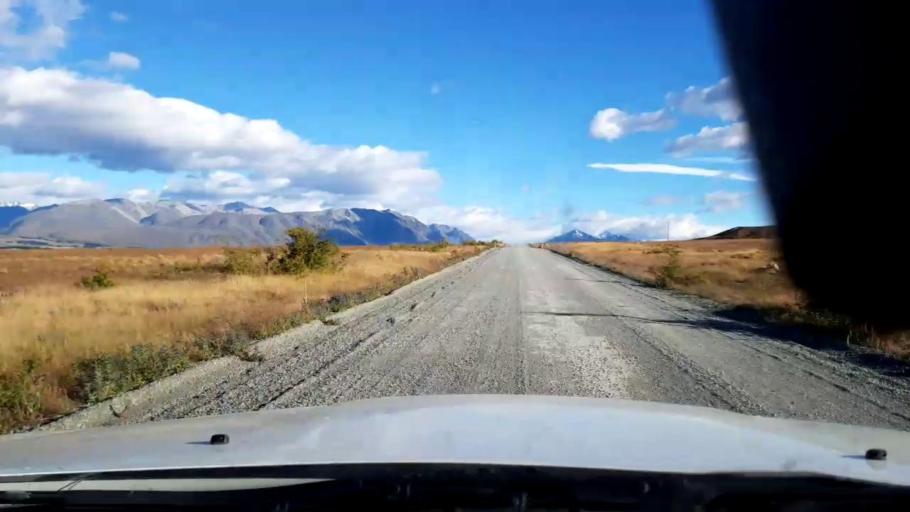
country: NZ
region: Canterbury
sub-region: Timaru District
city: Pleasant Point
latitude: -43.9222
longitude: 170.5597
